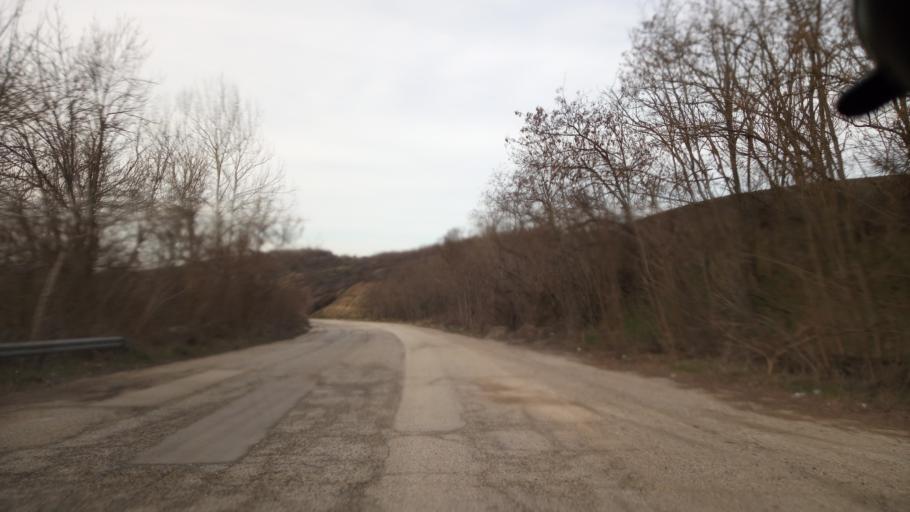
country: BG
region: Pleven
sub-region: Obshtina Nikopol
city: Nikopol
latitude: 43.5946
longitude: 24.9569
